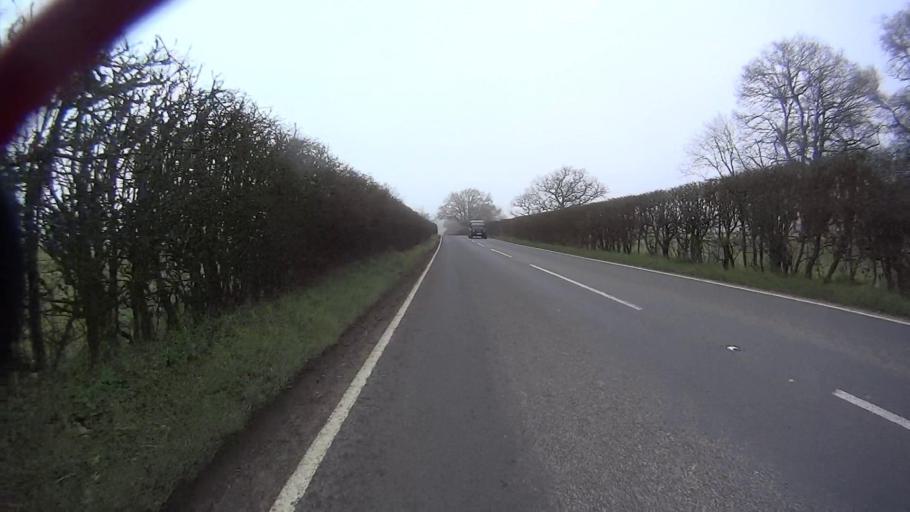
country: GB
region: England
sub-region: Surrey
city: Ockley
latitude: 51.1529
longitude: -0.3608
